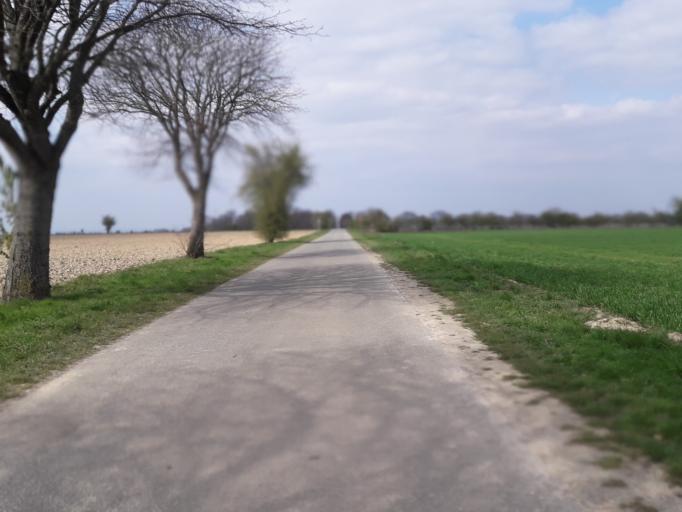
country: DE
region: North Rhine-Westphalia
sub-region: Regierungsbezirk Detmold
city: Paderborn
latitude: 51.6841
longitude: 8.7682
